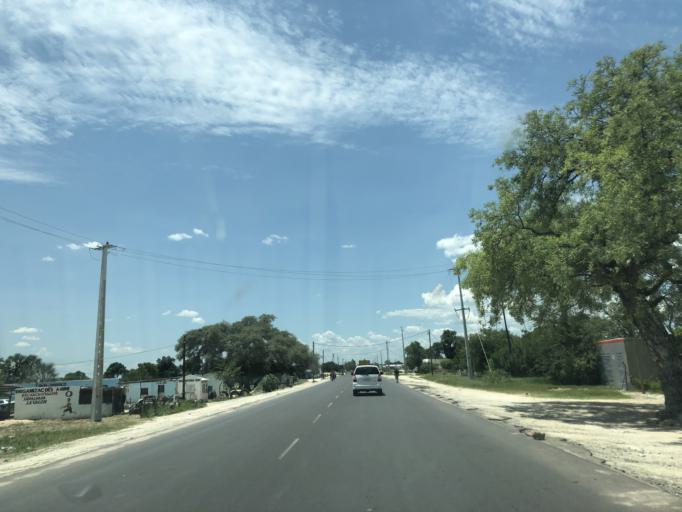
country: AO
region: Cunene
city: Ondjiva
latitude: -17.0620
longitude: 15.7385
